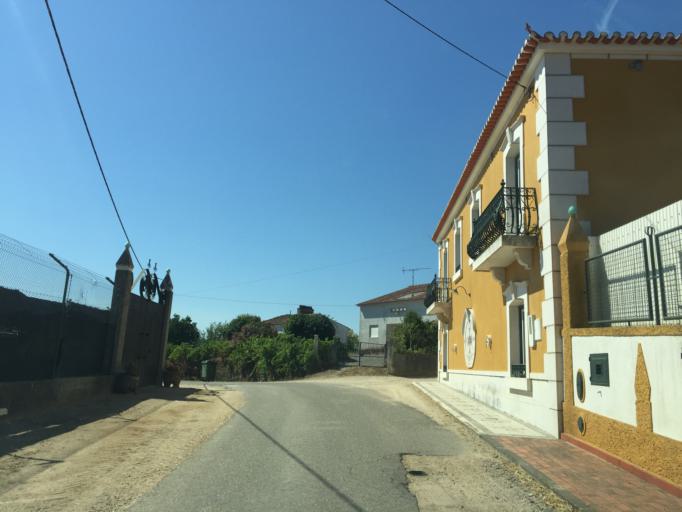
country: PT
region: Santarem
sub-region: Ferreira do Zezere
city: Ferreira do Zezere
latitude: 39.5880
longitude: -8.2789
